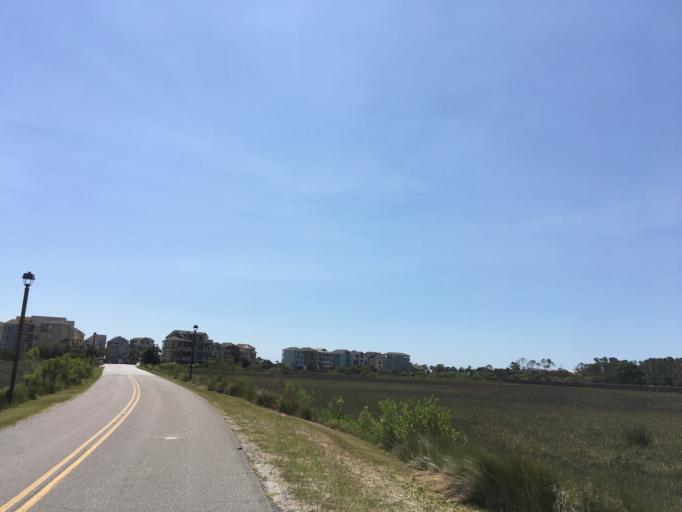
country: US
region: South Carolina
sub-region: Beaufort County
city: Hilton Head Island
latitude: 32.1910
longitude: -80.7031
